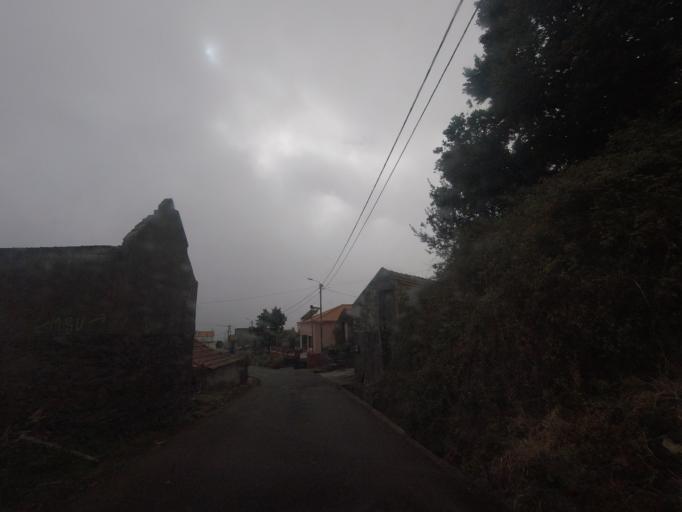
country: PT
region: Madeira
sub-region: Calheta
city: Faja da Ovelha
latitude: 32.7658
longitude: -17.2169
